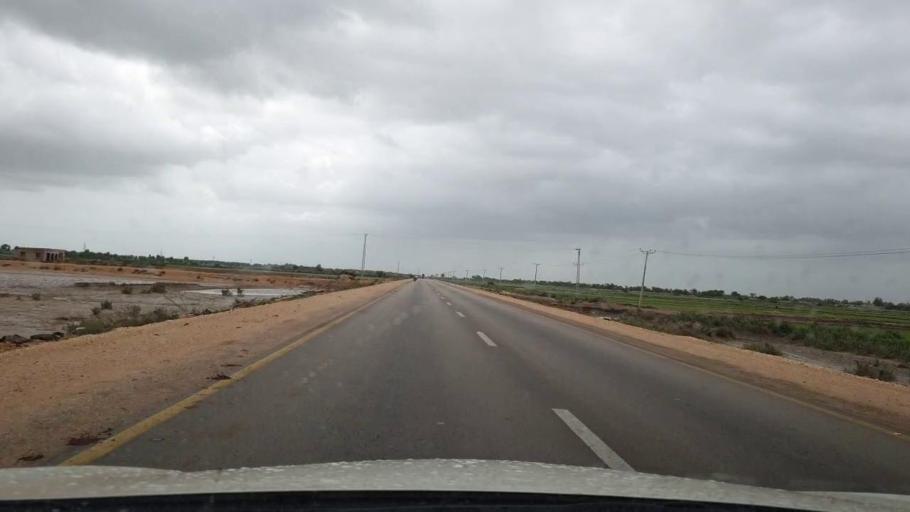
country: PK
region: Sindh
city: Badin
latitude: 24.6559
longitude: 68.7097
